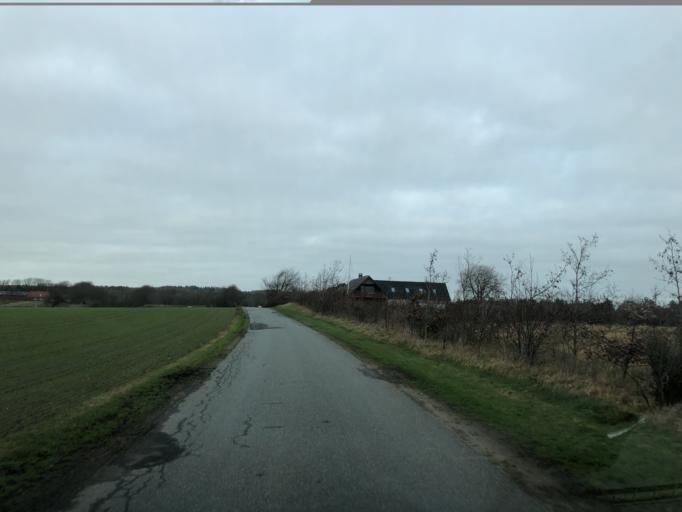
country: DK
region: Central Jutland
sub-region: Viborg Kommune
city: Stoholm
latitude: 56.4531
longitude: 9.1296
